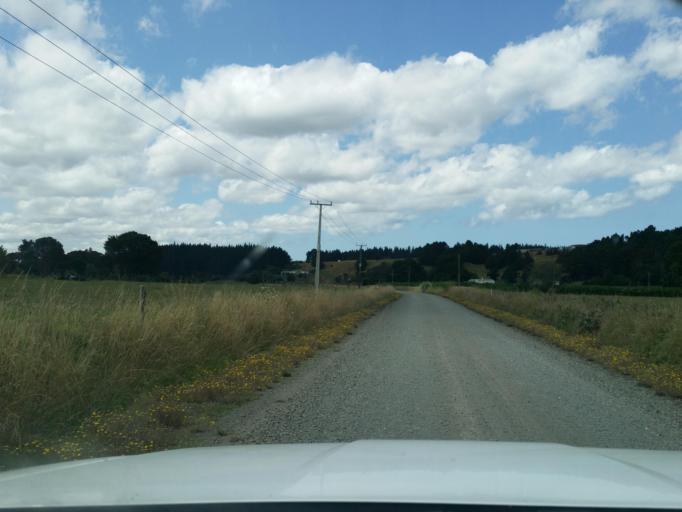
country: NZ
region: Northland
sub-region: Kaipara District
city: Dargaville
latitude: -35.8064
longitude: 173.7309
